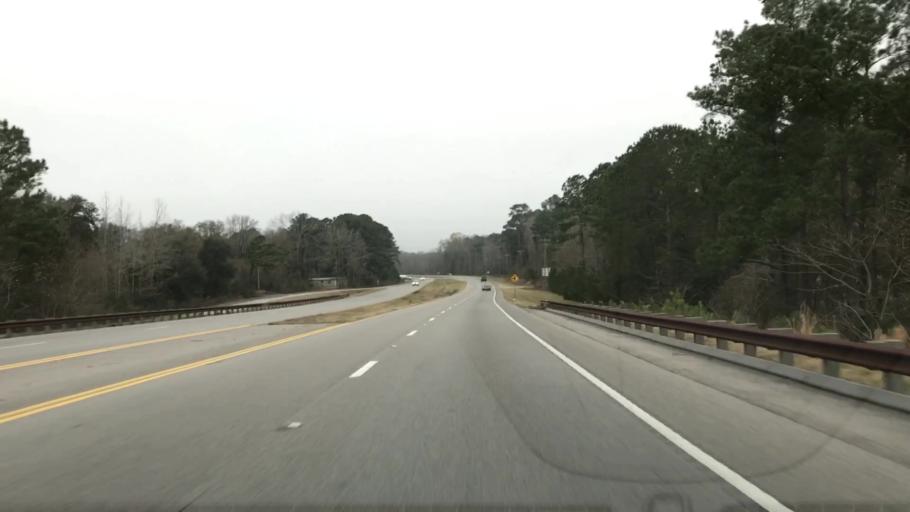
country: US
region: South Carolina
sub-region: Colleton County
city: Walterboro
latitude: 32.7331
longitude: -80.5944
